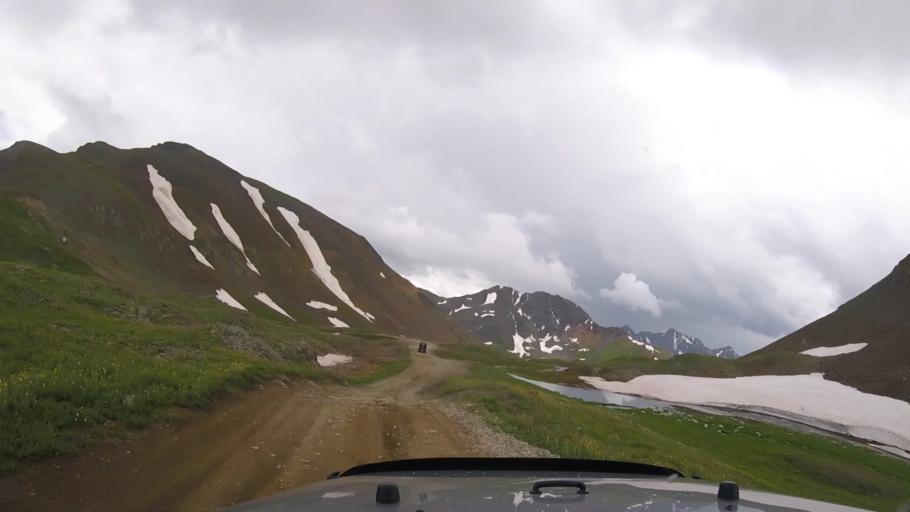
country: US
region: Colorado
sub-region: Ouray County
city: Ouray
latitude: 37.9188
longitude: -107.6291
